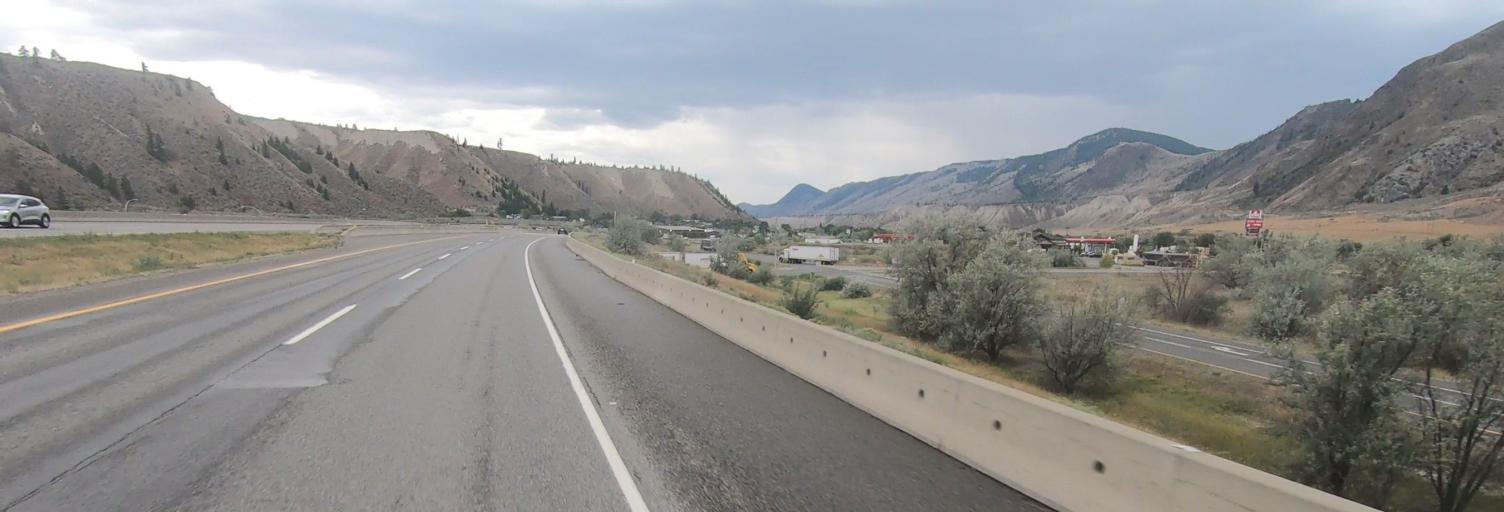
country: CA
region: British Columbia
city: Kamloops
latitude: 50.6596
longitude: -120.1159
